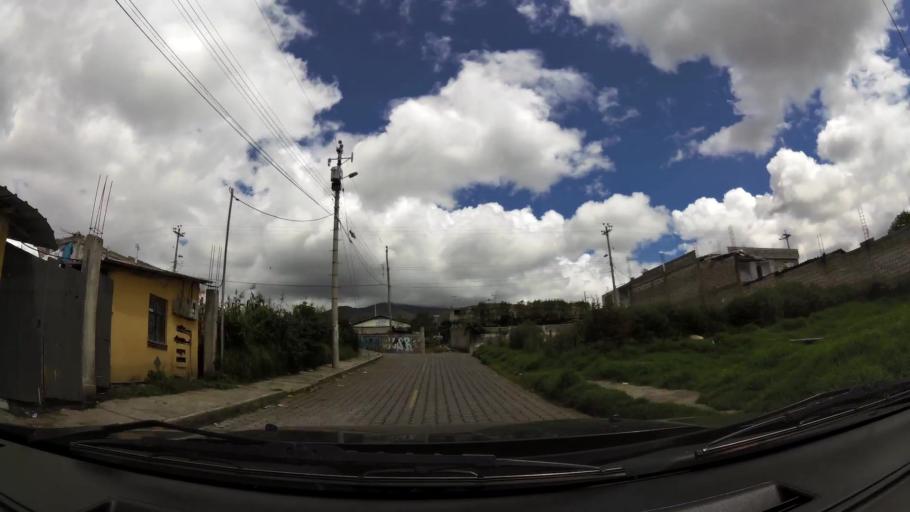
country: EC
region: Pichincha
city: Sangolqui
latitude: -0.3407
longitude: -78.5691
